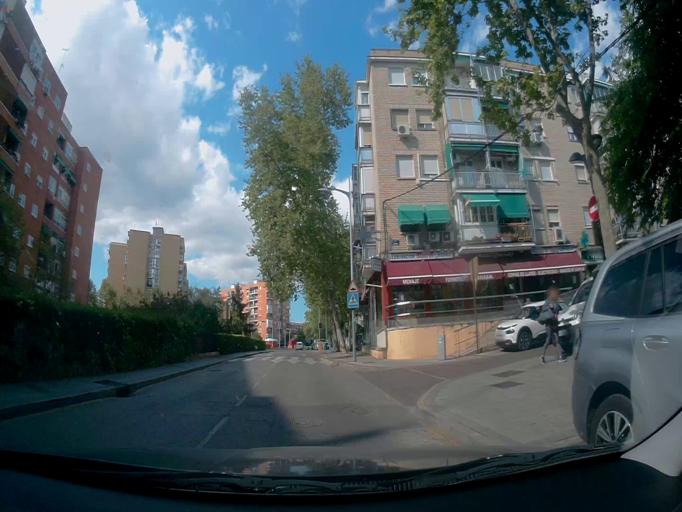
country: ES
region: Madrid
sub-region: Provincia de Madrid
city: Alcorcon
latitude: 40.3453
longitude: -3.8333
